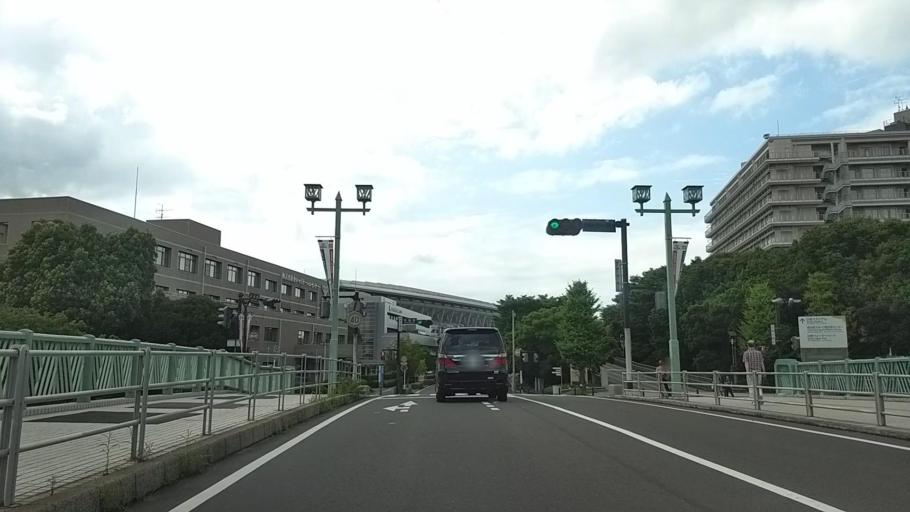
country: JP
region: Kanagawa
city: Yokohama
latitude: 35.5094
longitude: 139.6113
